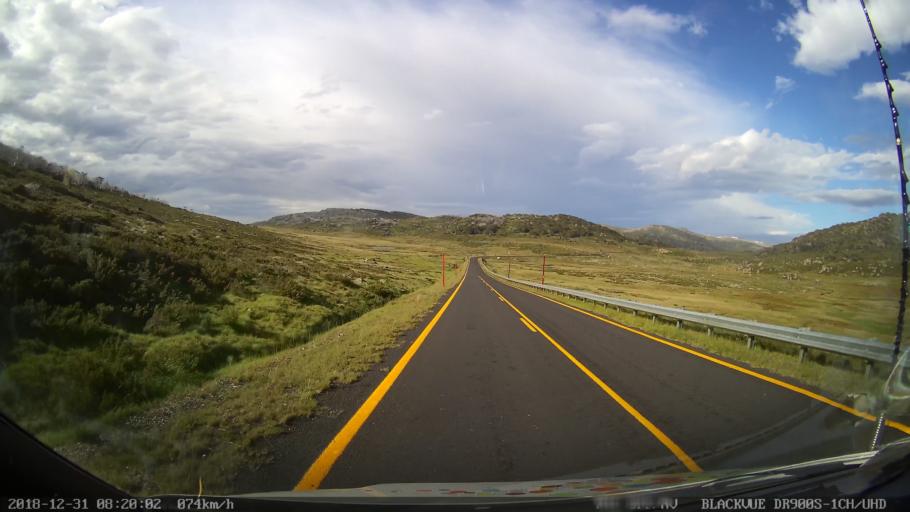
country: AU
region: New South Wales
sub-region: Snowy River
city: Jindabyne
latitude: -36.4229
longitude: 148.3791
